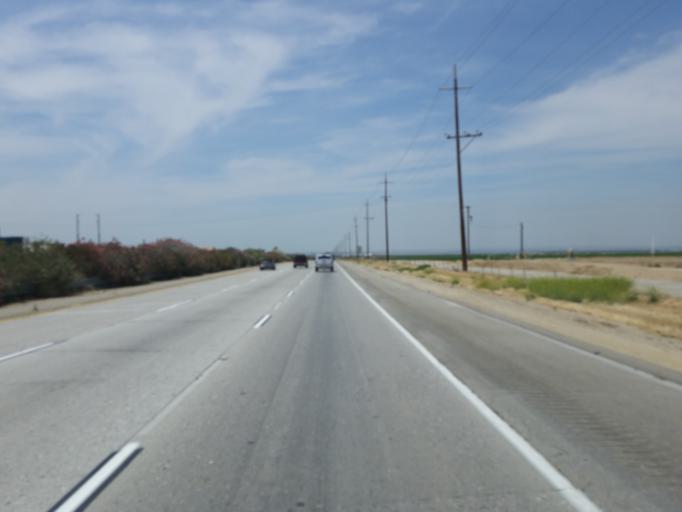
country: US
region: California
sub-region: Kern County
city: Weedpatch
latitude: 35.0609
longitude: -118.9687
